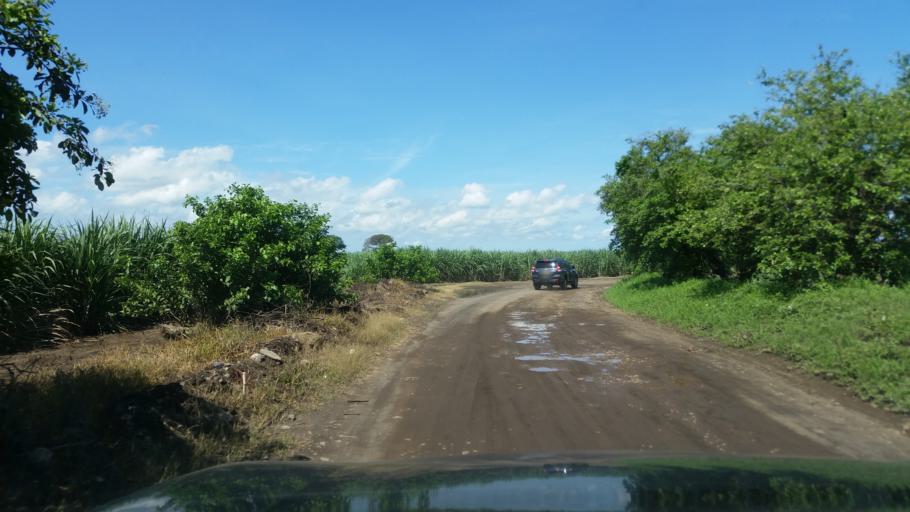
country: NI
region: Chinandega
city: Puerto Morazan
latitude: 12.7734
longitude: -87.1075
